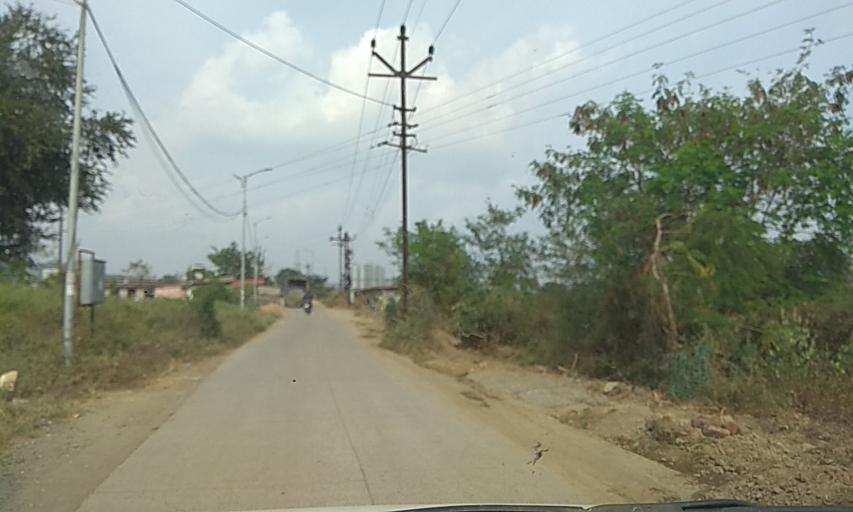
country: IN
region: Maharashtra
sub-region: Pune Division
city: Pimpri
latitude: 18.5842
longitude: 73.7058
